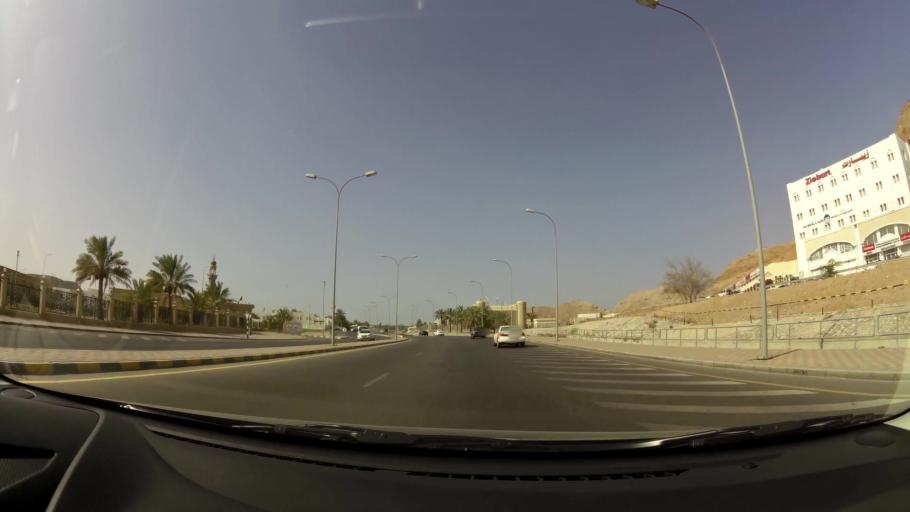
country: OM
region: Muhafazat Masqat
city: Muscat
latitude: 23.6076
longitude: 58.5126
